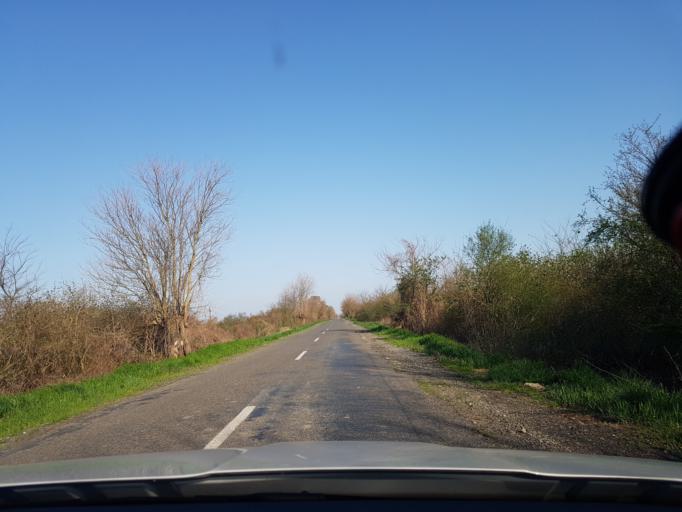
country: HU
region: Tolna
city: Ocseny
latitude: 46.3349
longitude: 18.8019
